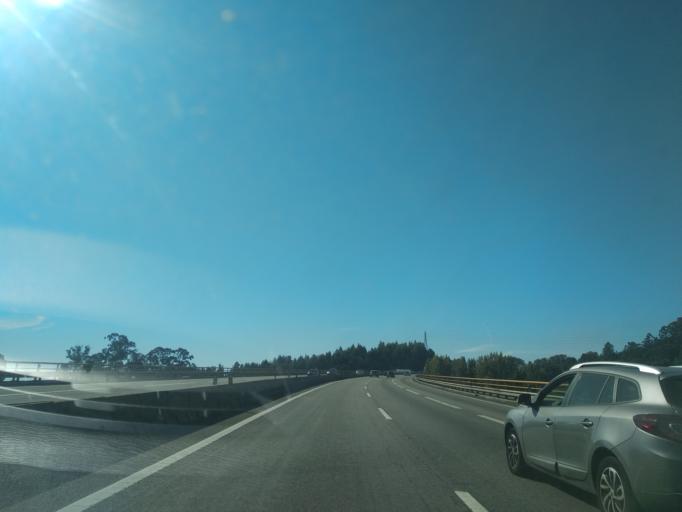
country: PT
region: Porto
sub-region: Vila Nova de Gaia
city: Perozinho
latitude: 41.0813
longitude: -8.5754
